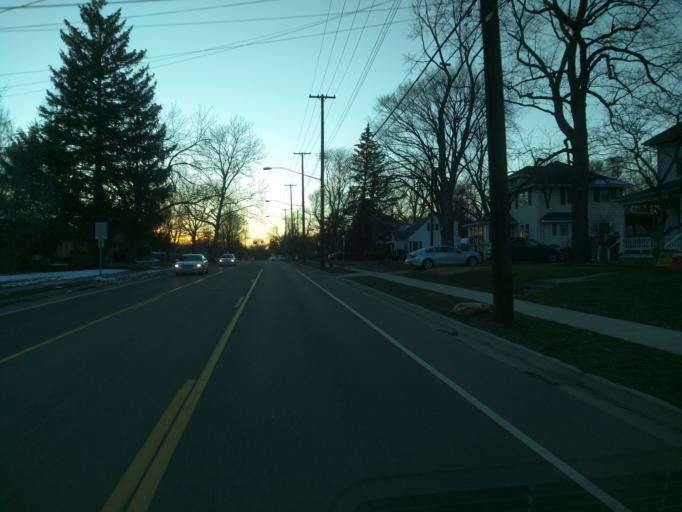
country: US
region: Michigan
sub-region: Ingham County
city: Lansing
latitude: 42.6974
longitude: -84.5507
